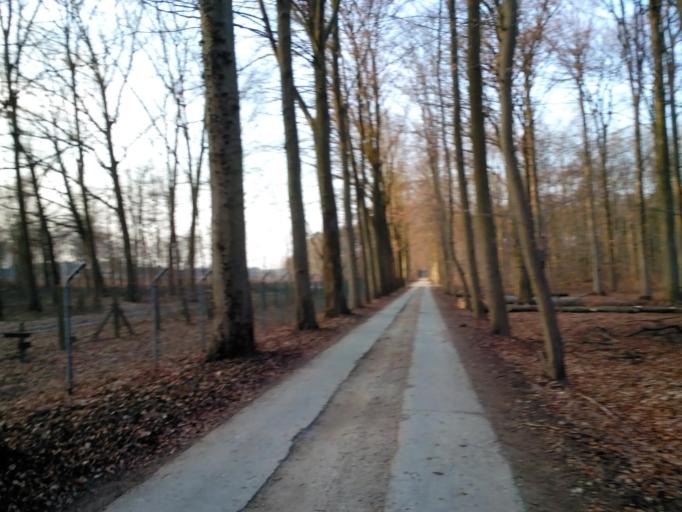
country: BE
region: Flanders
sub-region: Provincie Vlaams-Brabant
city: Oud-Heverlee
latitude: 50.8165
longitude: 4.6959
